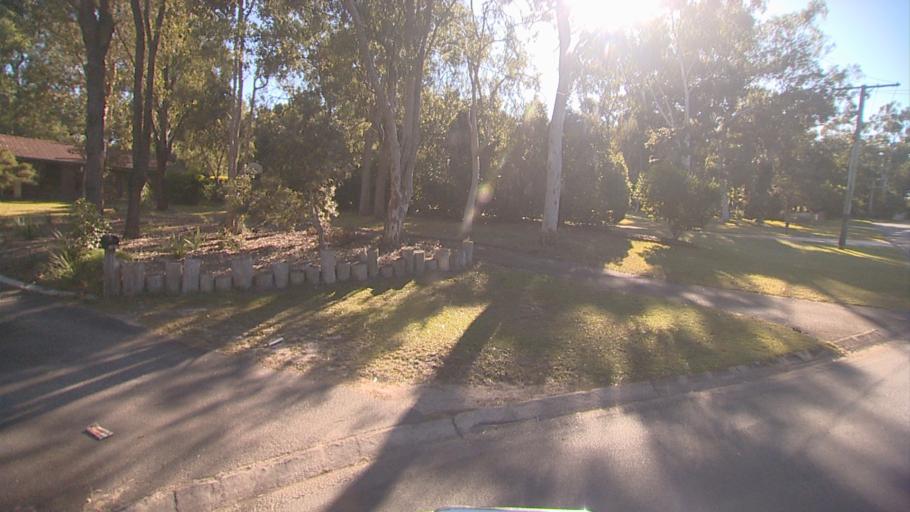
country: AU
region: Queensland
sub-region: Brisbane
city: Forest Lake
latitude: -27.6696
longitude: 153.0069
